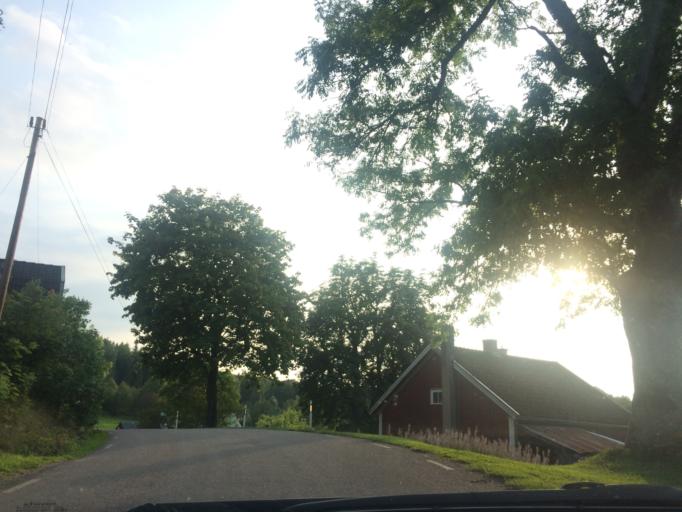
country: SE
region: Vaestra Goetaland
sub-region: Alingsas Kommun
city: Alingsas
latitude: 58.0154
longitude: 12.5266
